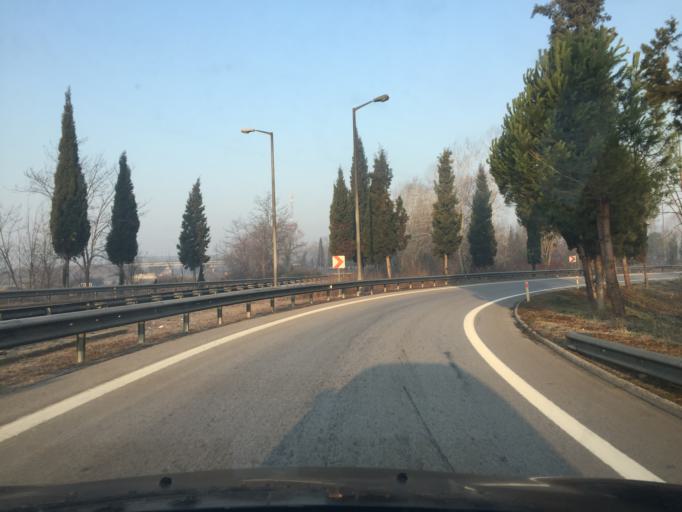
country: TR
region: Sakarya
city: Akyazi
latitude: 40.7157
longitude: 30.5672
